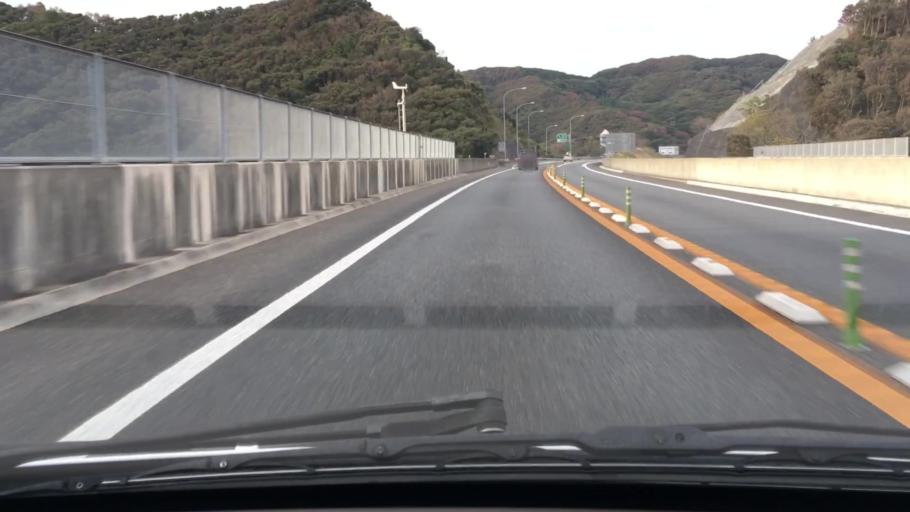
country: JP
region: Chiba
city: Futtsu
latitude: 35.1661
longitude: 139.8310
